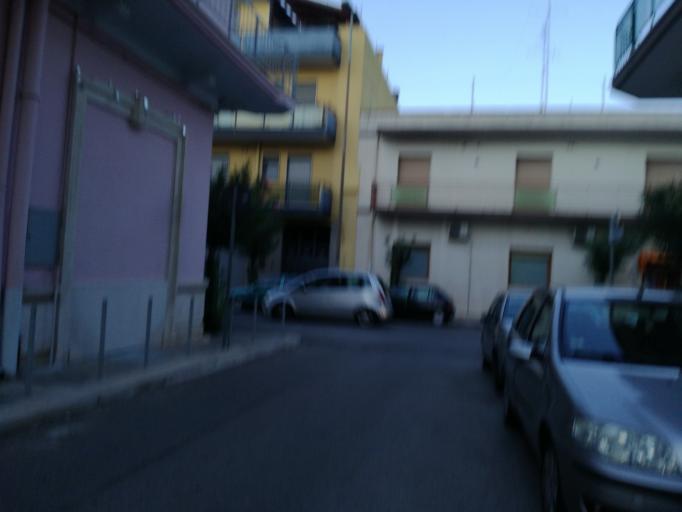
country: IT
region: Apulia
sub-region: Provincia di Bari
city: Triggiano
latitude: 41.0638
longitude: 16.9278
